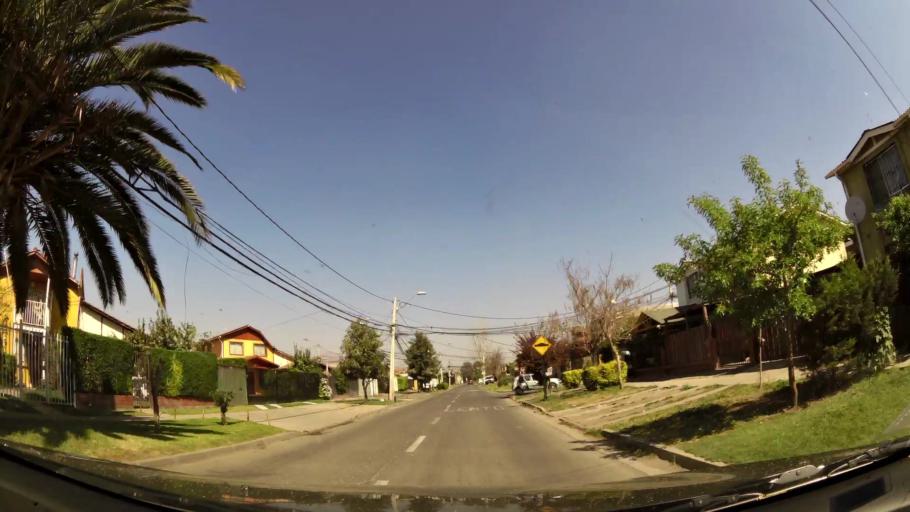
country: CL
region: Santiago Metropolitan
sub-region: Provincia de Santiago
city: Lo Prado
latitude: -33.3495
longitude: -70.7345
